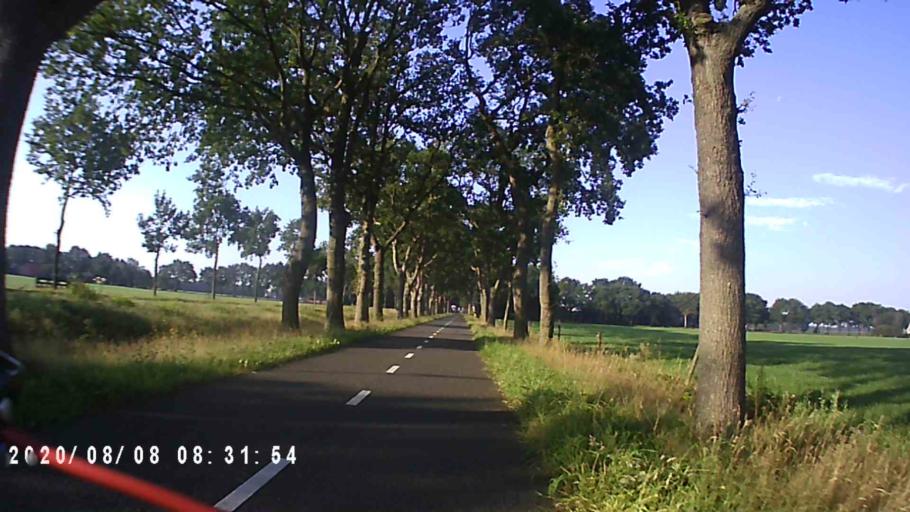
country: NL
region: Groningen
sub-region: Gemeente Leek
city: Leek
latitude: 53.0774
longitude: 6.3340
